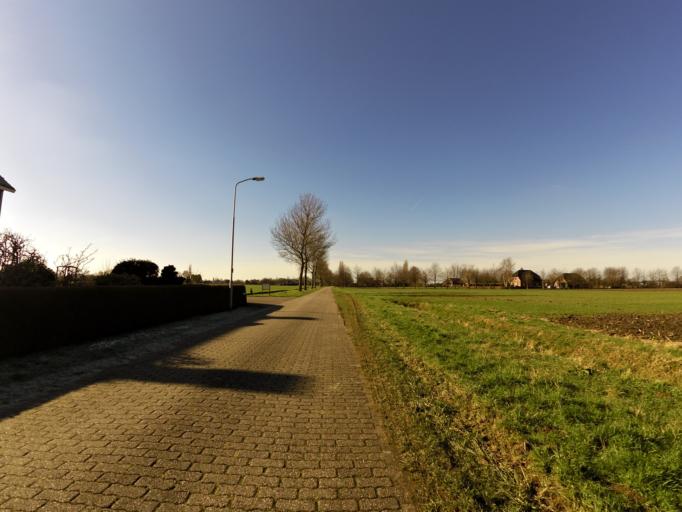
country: NL
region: Gelderland
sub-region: Gemeente Doesburg
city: Doesburg
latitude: 51.9404
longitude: 6.1671
